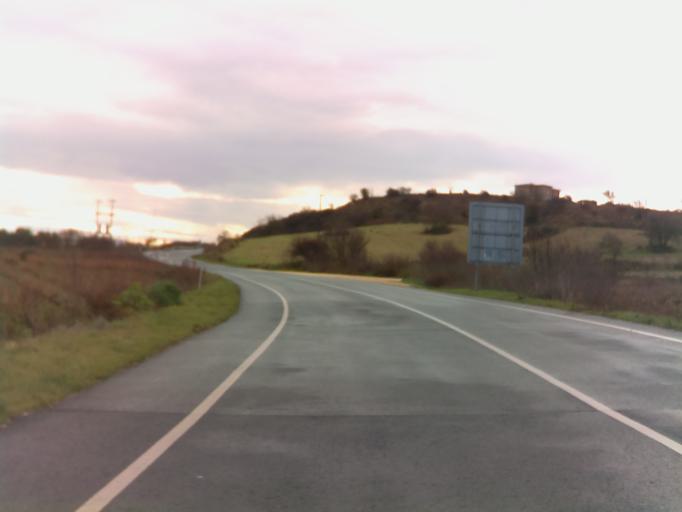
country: CY
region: Pafos
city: Pegeia
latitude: 34.9079
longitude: 32.4380
